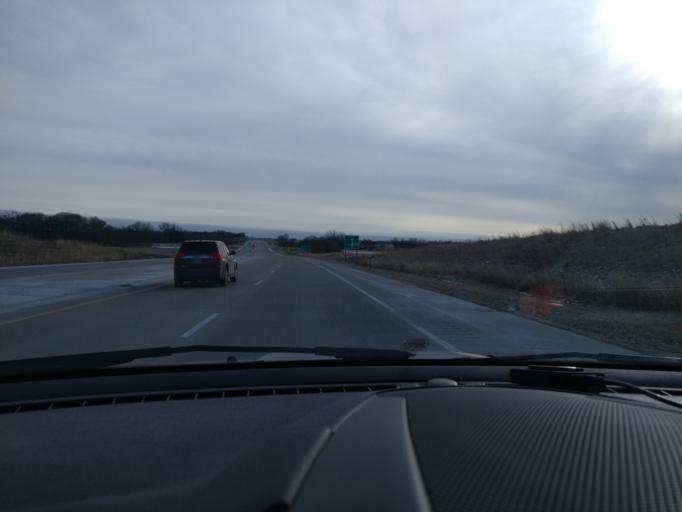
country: US
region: Nebraska
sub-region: Saunders County
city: Wahoo
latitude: 41.2110
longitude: -96.6373
